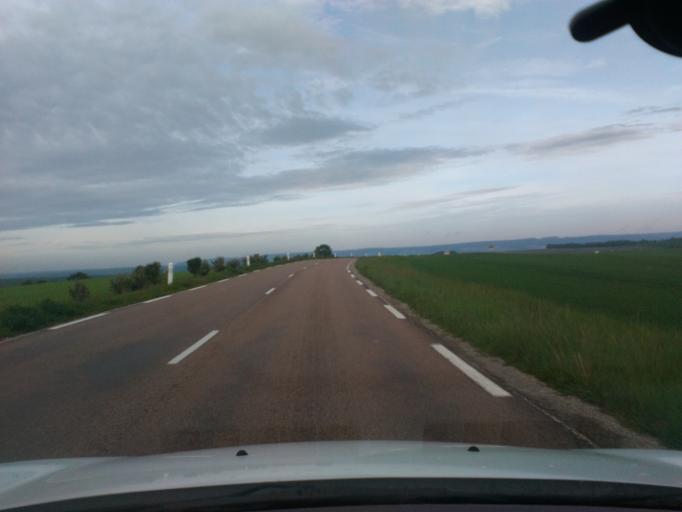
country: FR
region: Champagne-Ardenne
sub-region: Departement de l'Aube
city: Ville-sous-la-Ferte
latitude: 48.2178
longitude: 4.8314
